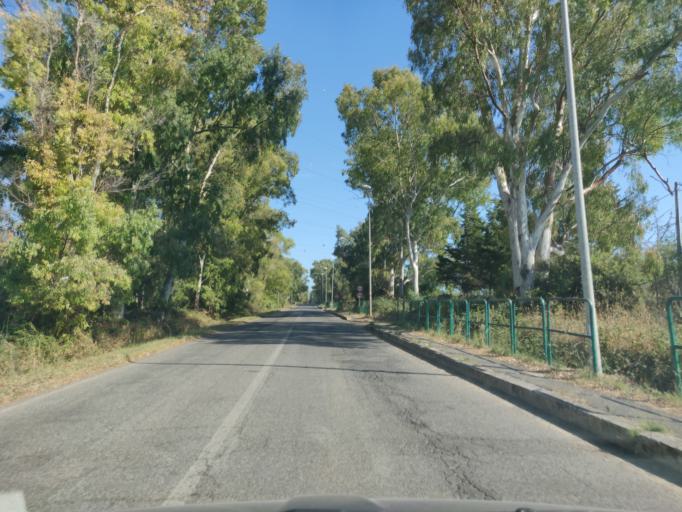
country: IT
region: Latium
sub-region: Citta metropolitana di Roma Capitale
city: Aurelia
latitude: 42.1396
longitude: 11.7668
